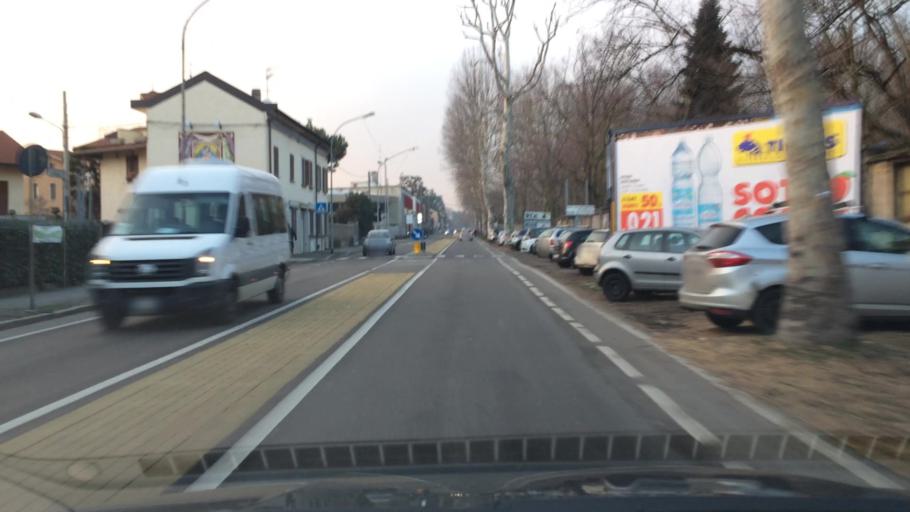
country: IT
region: Lombardy
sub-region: Provincia di Varese
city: Saronno
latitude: 45.6194
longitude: 9.0300
